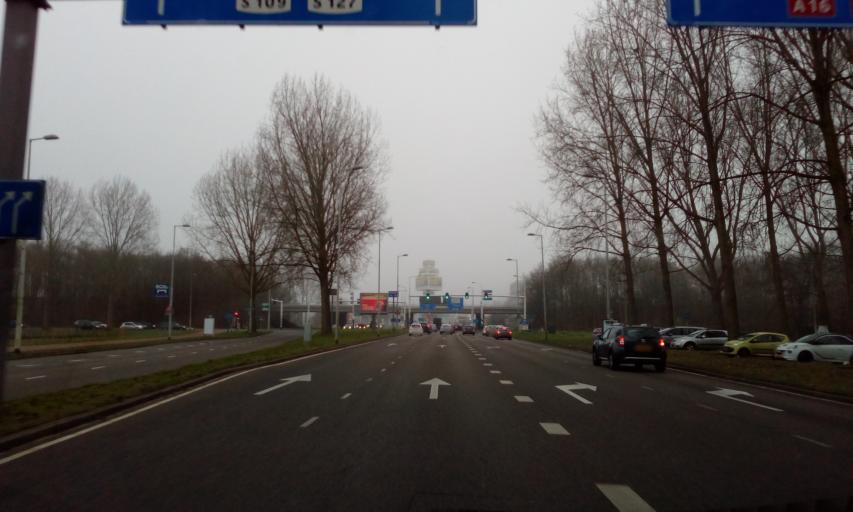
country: NL
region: South Holland
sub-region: Gemeente Capelle aan den IJssel
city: Capelle aan den IJssel
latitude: 51.9577
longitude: 4.5616
